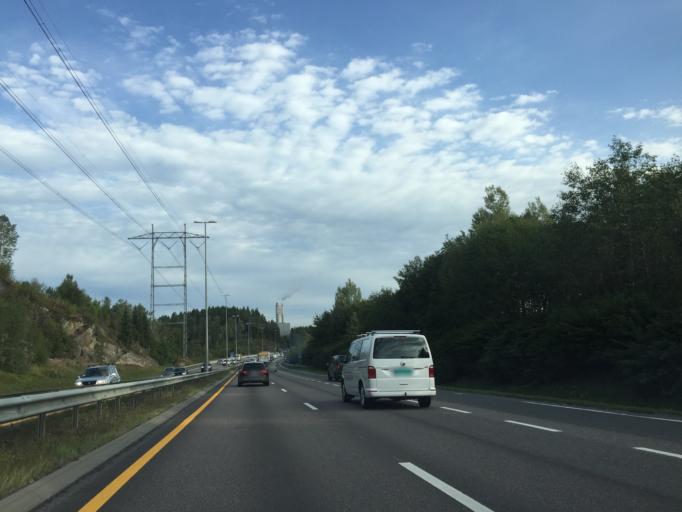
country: NO
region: Akershus
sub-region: Oppegard
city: Kolbotn
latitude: 59.8320
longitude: 10.8413
